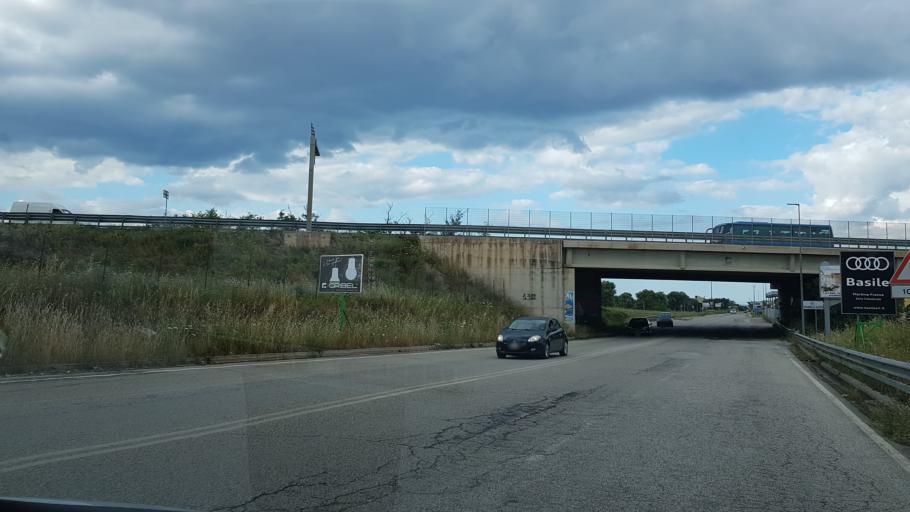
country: IT
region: Apulia
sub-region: Provincia di Brindisi
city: Fasano
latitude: 40.8401
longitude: 17.3714
